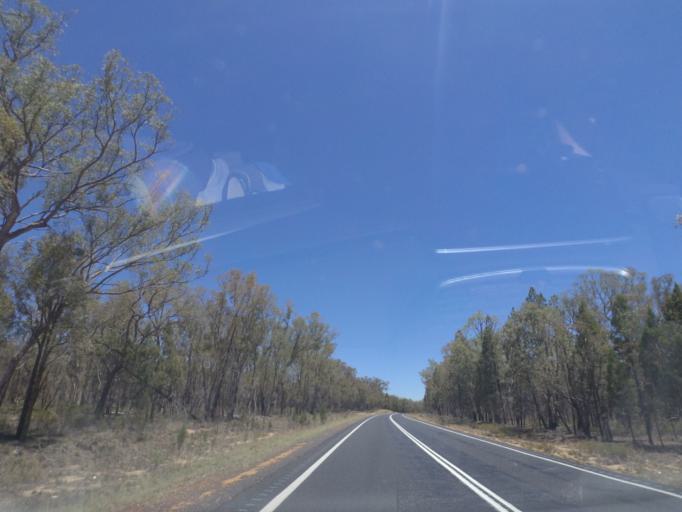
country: AU
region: New South Wales
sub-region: Warrumbungle Shire
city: Coonabarabran
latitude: -31.1917
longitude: 149.3534
